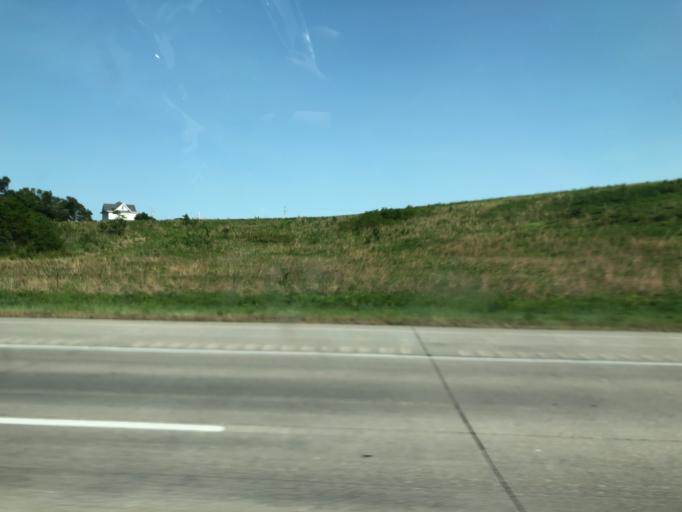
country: US
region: Nebraska
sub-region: Saunders County
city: Ashland
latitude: 40.9579
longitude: -96.4093
